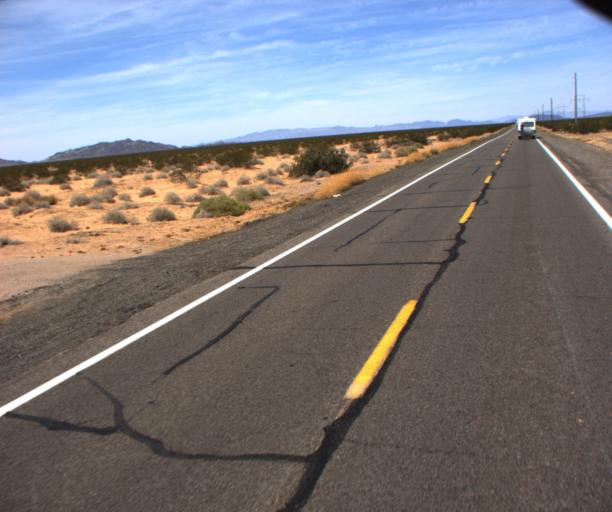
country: US
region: Arizona
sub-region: La Paz County
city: Parker
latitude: 33.9133
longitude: -114.2169
